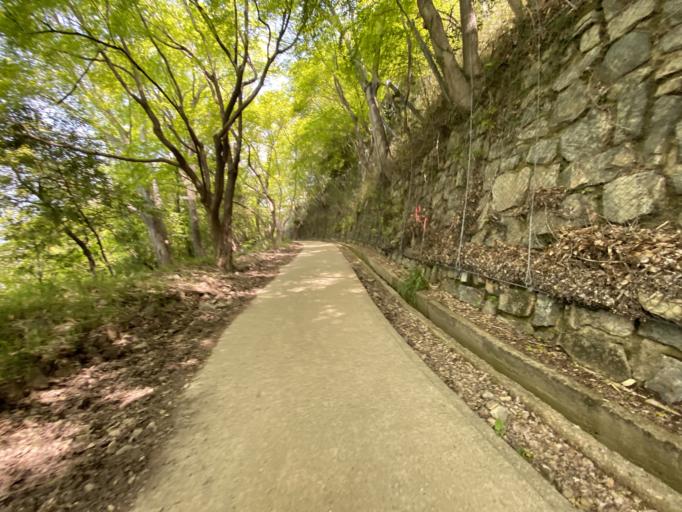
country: JP
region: Hyogo
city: Ashiya
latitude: 34.7329
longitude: 135.2762
